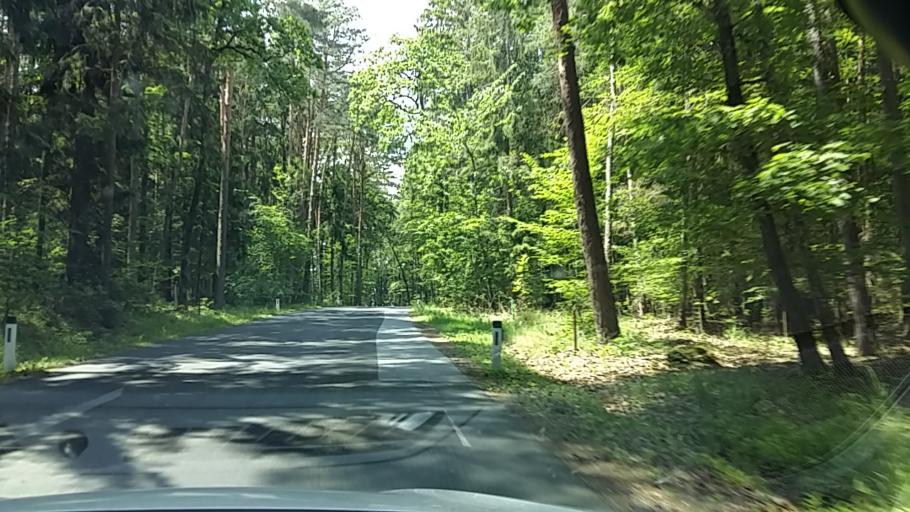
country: AT
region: Styria
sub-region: Politischer Bezirk Hartberg-Fuerstenfeld
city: Bad Blumau
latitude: 47.1203
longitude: 16.0414
